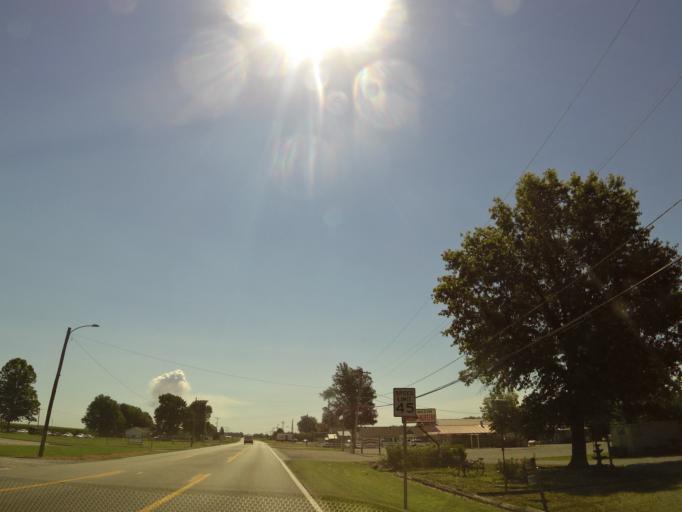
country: US
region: Arkansas
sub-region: Clay County
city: Piggott
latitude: 36.3817
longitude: -90.1770
